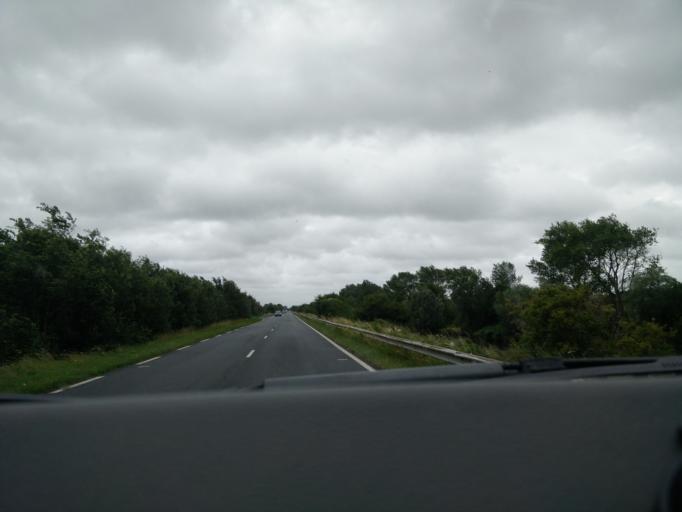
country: FR
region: Nord-Pas-de-Calais
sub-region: Departement du Nord
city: Zuydcoote
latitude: 51.0574
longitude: 2.4898
